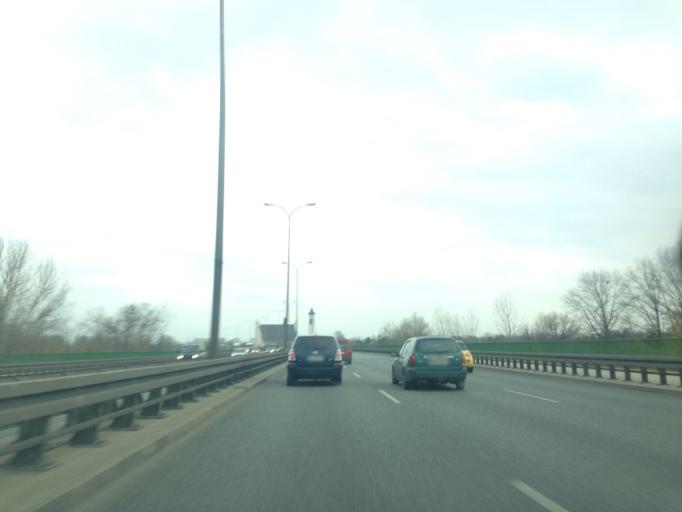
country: PL
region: Masovian Voivodeship
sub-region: Warszawa
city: Praga Poludnie
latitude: 52.2126
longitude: 21.0897
